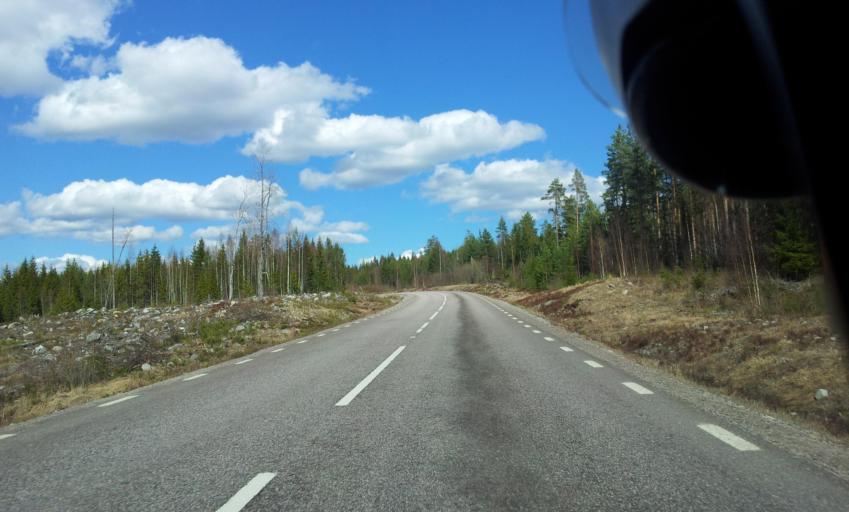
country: SE
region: Gaevleborg
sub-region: Ovanakers Kommun
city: Edsbyn
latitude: 61.2144
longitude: 15.8746
